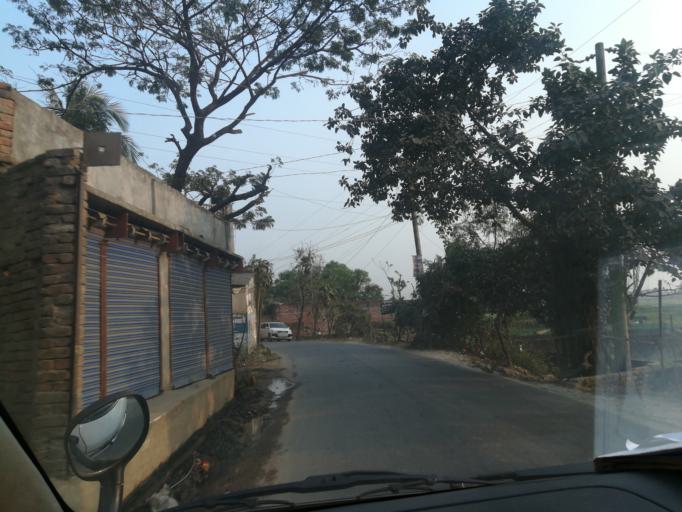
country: BD
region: Dhaka
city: Tungi
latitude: 23.8565
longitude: 90.3283
